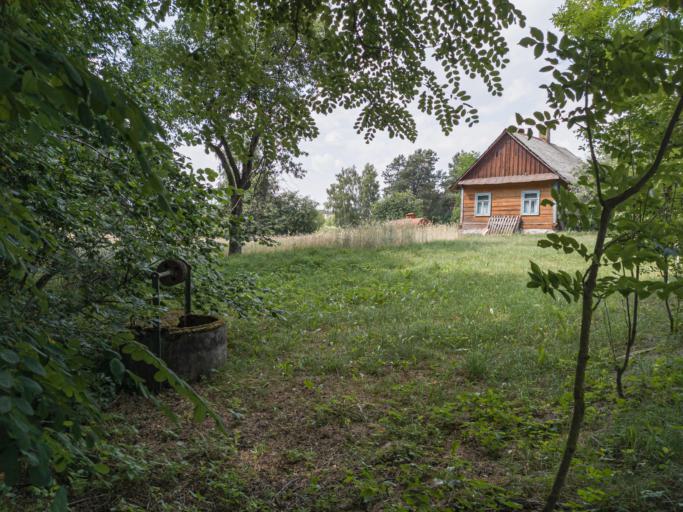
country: BY
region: Brest
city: Kamyanyets
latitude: 52.3930
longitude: 23.8847
